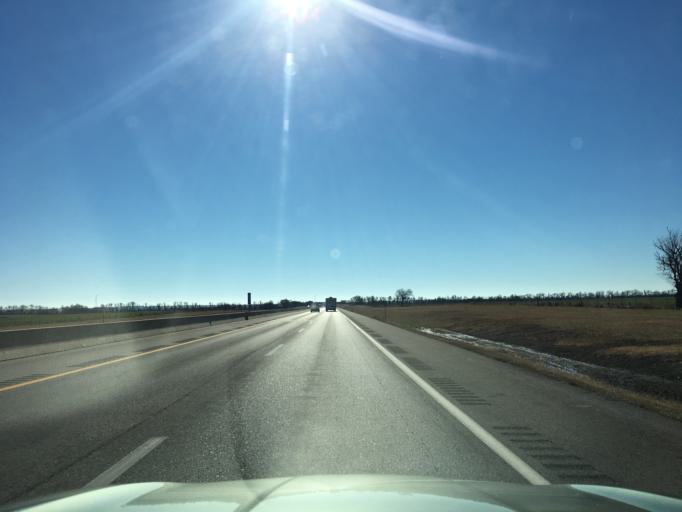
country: US
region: Kansas
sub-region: Sumner County
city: Wellington
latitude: 37.0429
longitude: -97.3384
